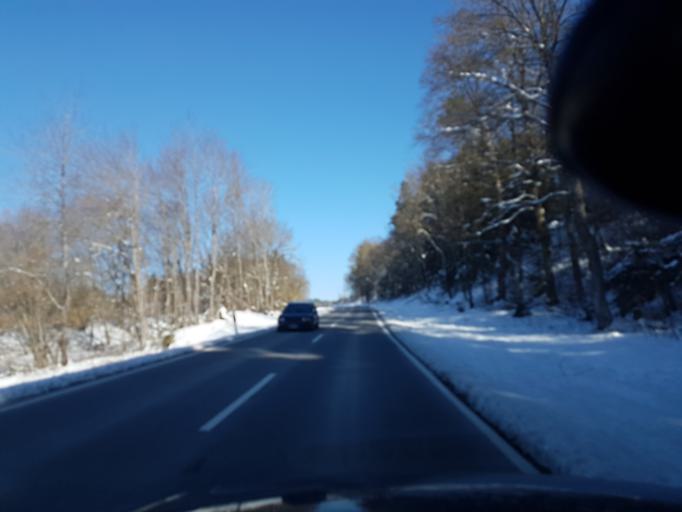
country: DE
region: Baden-Wuerttemberg
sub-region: Freiburg Region
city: Niedereschach
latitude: 48.1680
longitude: 8.5492
